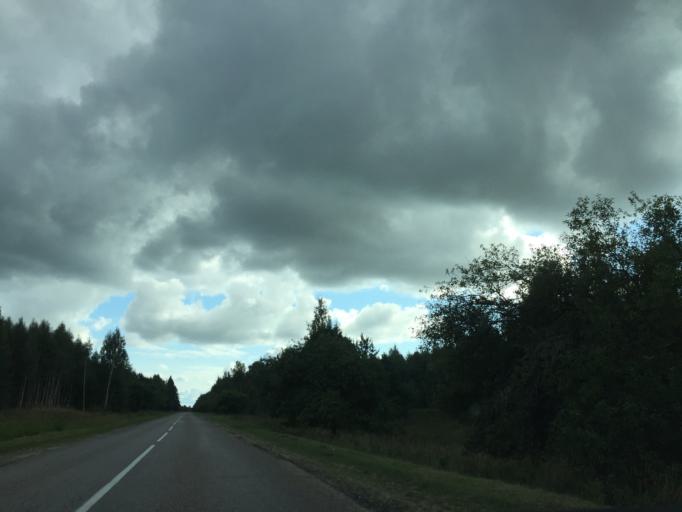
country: LV
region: Limbazu Rajons
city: Limbazi
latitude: 57.3649
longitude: 24.6716
